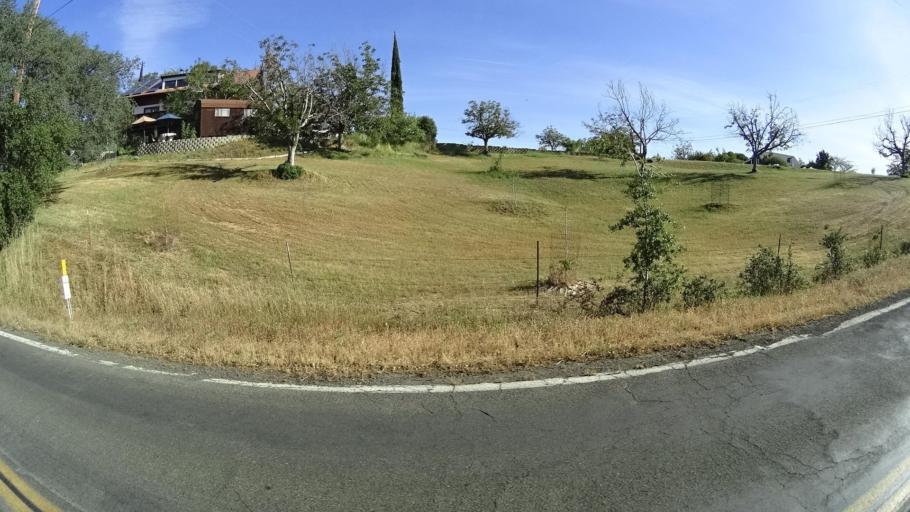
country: US
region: California
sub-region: Lake County
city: Lakeport
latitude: 39.0405
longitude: -122.9352
